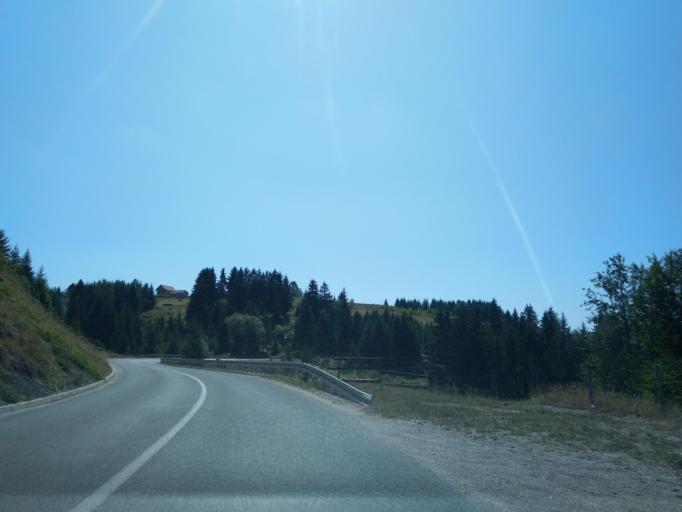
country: RS
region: Central Serbia
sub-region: Zlatiborski Okrug
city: Nova Varos
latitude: 43.4332
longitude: 19.8262
